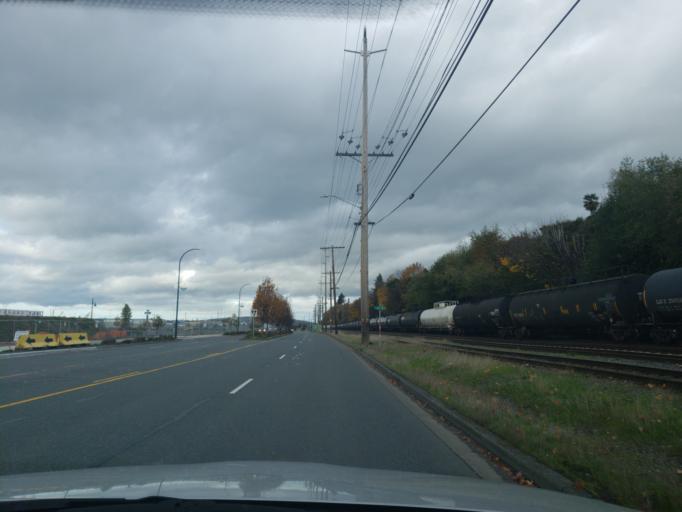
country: US
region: Washington
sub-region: Snohomish County
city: Everett
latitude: 47.9970
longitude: -122.2137
